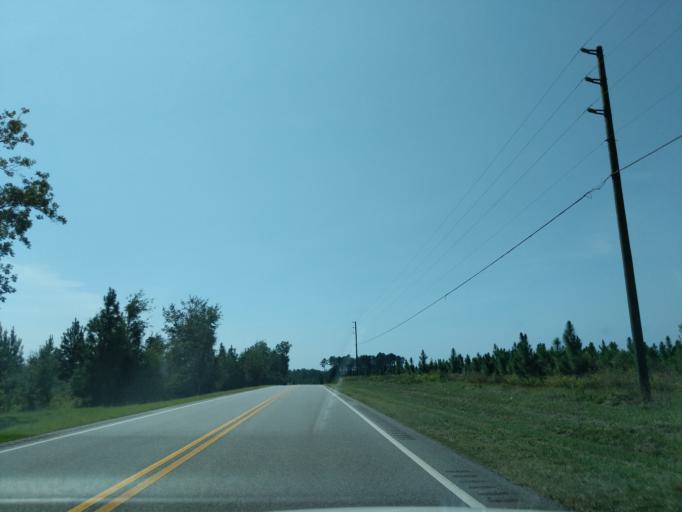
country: US
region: Alabama
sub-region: Covington County
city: Andalusia
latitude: 31.2071
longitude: -86.5491
